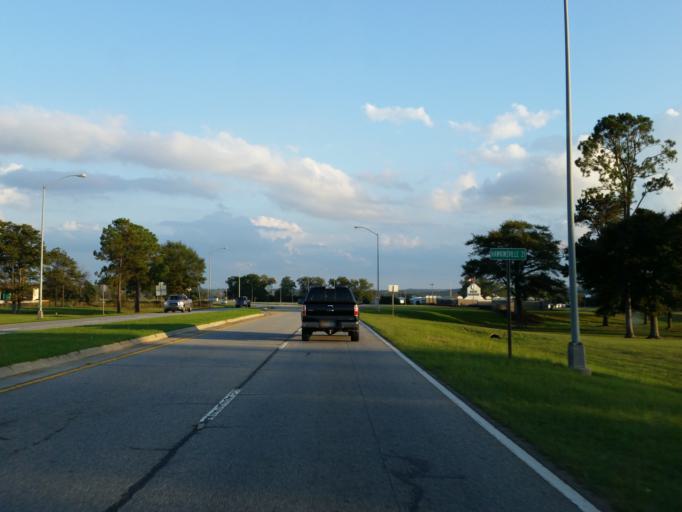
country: US
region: Georgia
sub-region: Houston County
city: Perry
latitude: 32.4450
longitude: -83.7503
